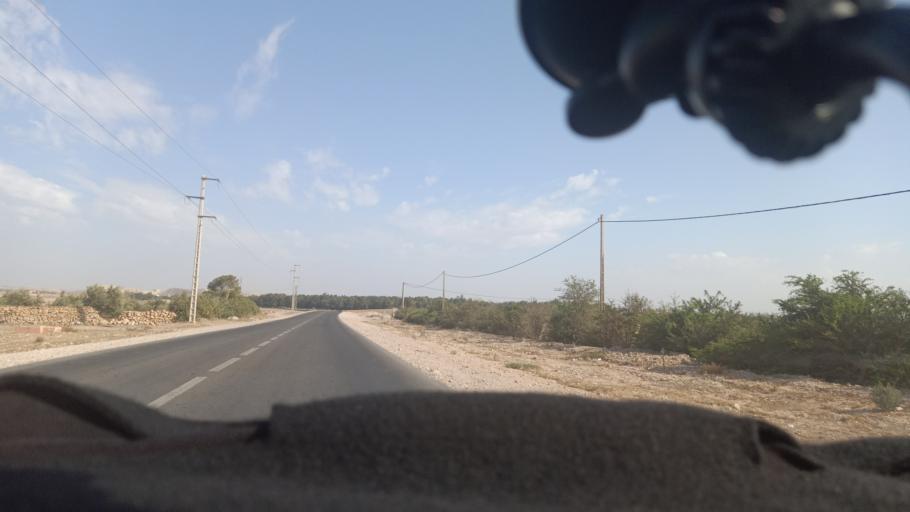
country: MA
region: Doukkala-Abda
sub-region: Safi
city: Youssoufia
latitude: 32.2788
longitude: -8.5448
